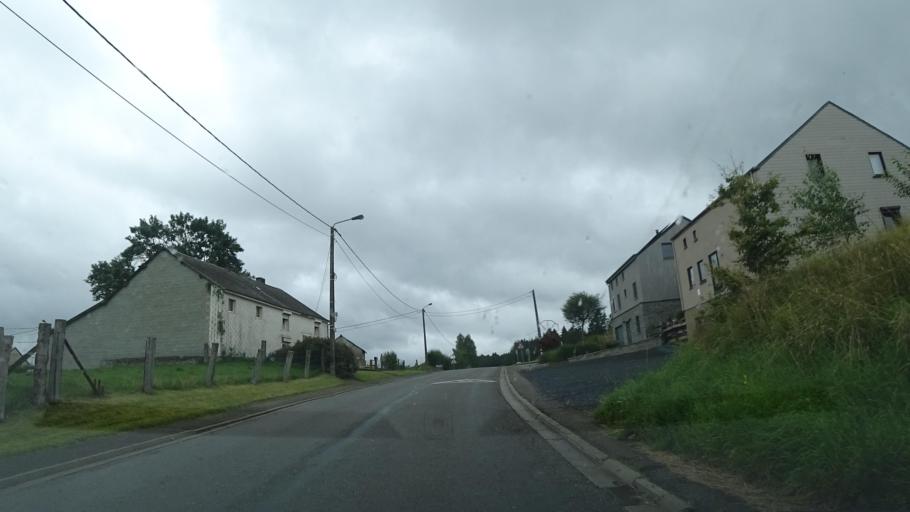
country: BE
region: Wallonia
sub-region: Province du Luxembourg
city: Chiny
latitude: 49.8069
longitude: 5.3280
